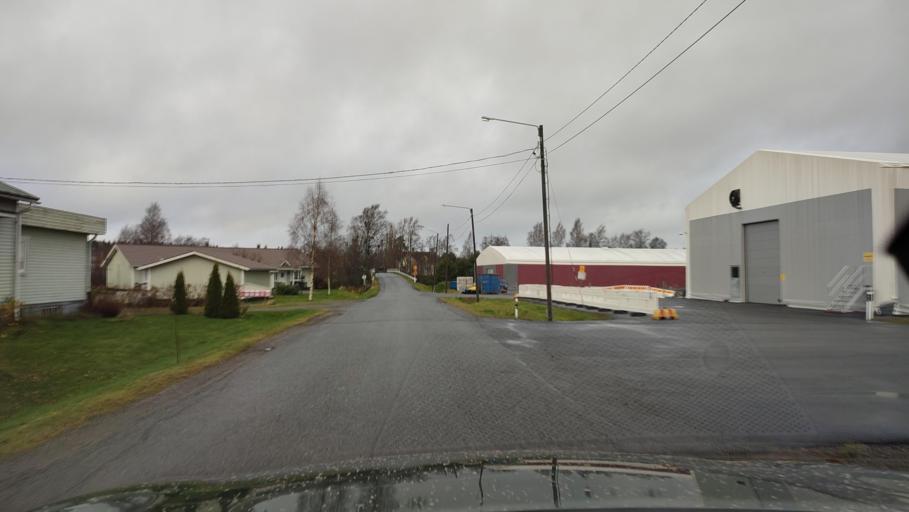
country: FI
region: Ostrobothnia
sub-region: Sydosterbotten
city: Kristinestad
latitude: 62.3013
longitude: 21.4556
